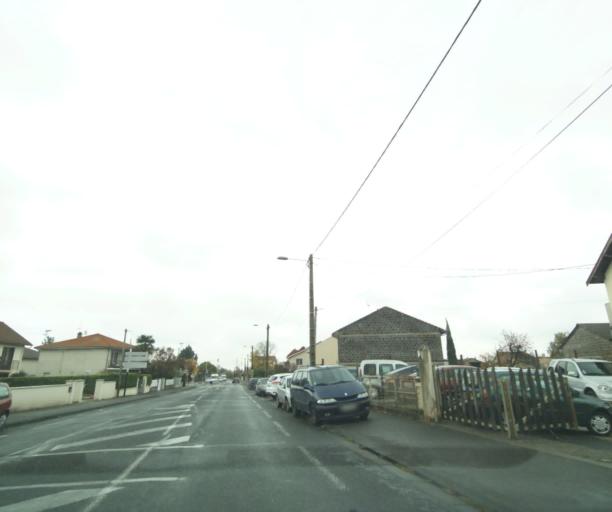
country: FR
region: Auvergne
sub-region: Departement du Puy-de-Dome
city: Aubiere
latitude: 45.7552
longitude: 3.1164
